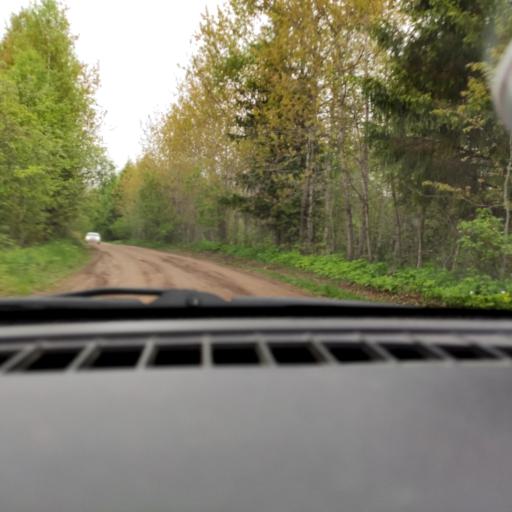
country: RU
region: Perm
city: Polazna
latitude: 58.2926
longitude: 56.1414
